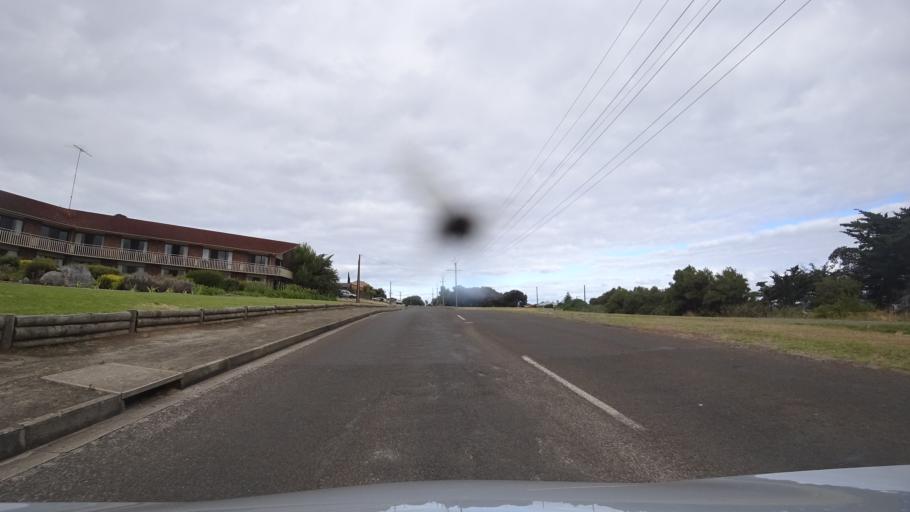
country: AU
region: South Australia
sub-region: Kangaroo Island
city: Kingscote
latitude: -35.6602
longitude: 137.6309
